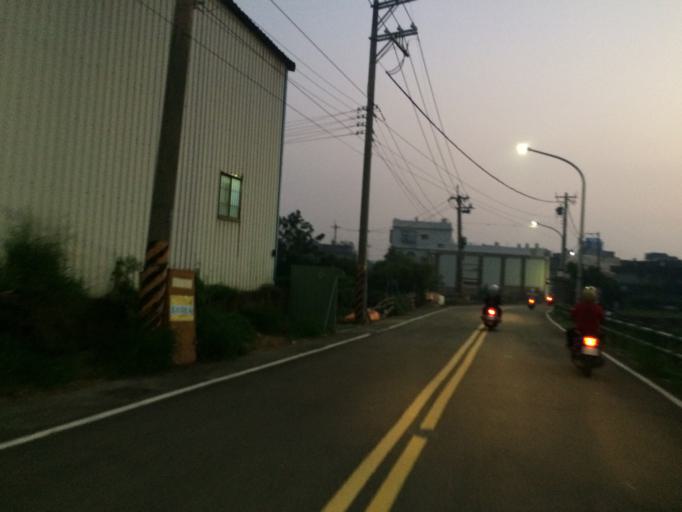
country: TW
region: Taiwan
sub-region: Hsinchu
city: Hsinchu
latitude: 24.7754
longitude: 120.9169
